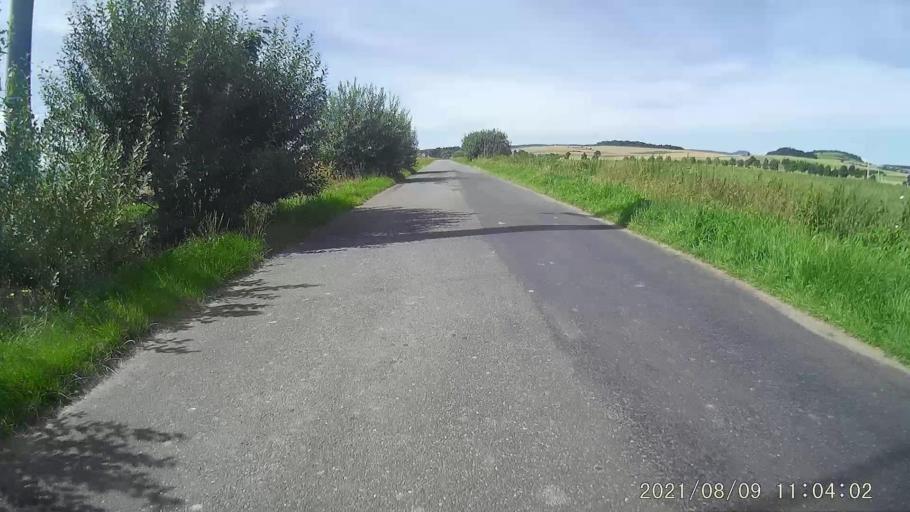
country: PL
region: Lower Silesian Voivodeship
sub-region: Powiat klodzki
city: Bozkow
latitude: 50.4632
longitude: 16.5677
